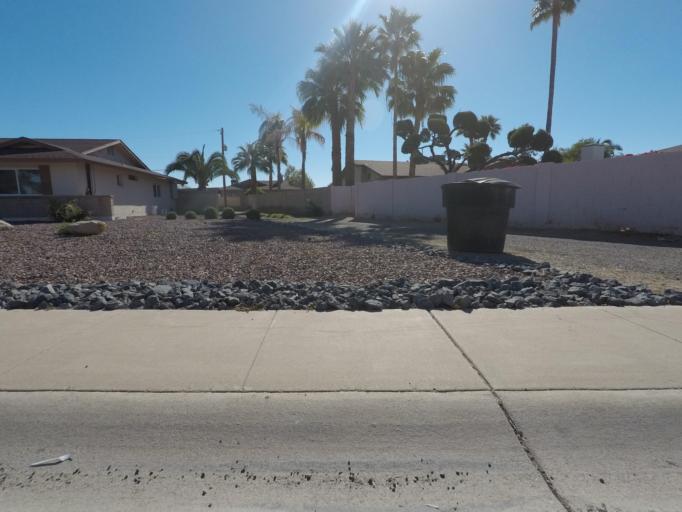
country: US
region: Arizona
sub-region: Maricopa County
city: Glendale
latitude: 33.5407
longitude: -112.1218
